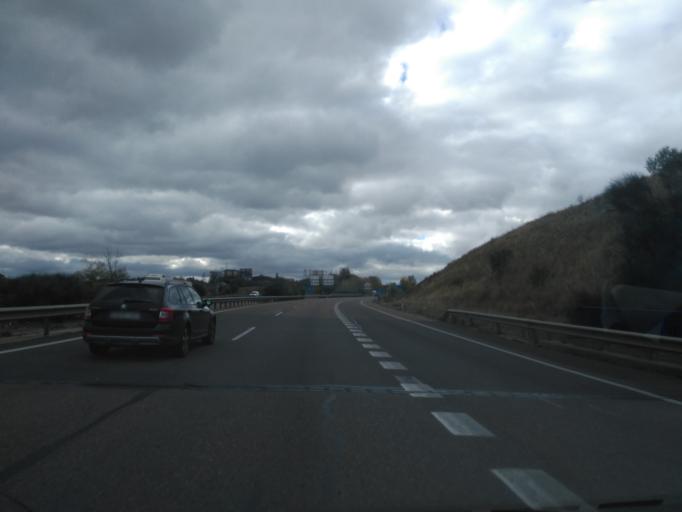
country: ES
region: Castille and Leon
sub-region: Provincia de Valladolid
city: Valladolid
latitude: 41.6843
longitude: -4.7305
